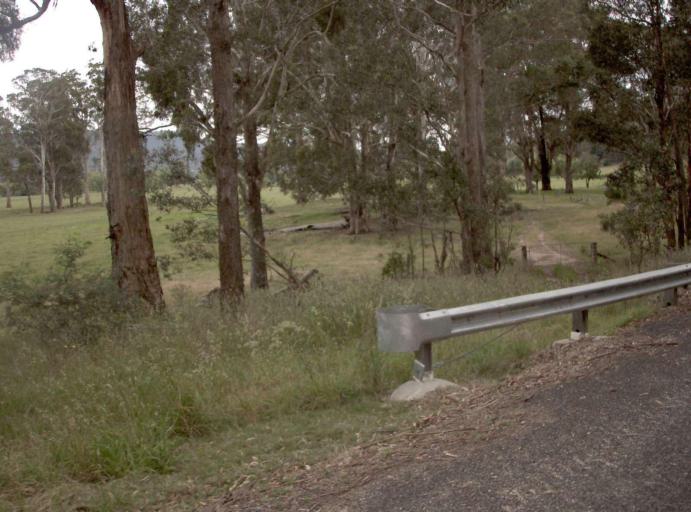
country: AU
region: New South Wales
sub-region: Bombala
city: Bombala
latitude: -37.5074
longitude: 149.1746
